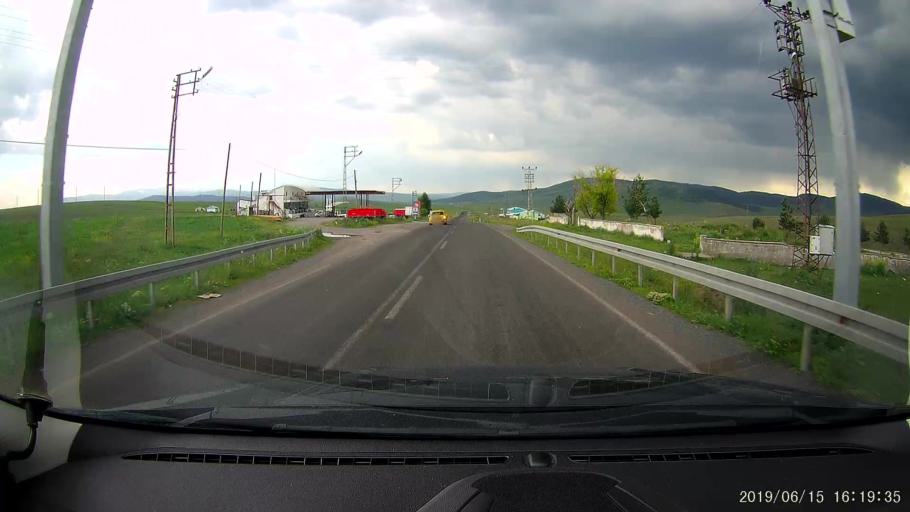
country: TR
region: Ardahan
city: Hanak
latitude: 41.2268
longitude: 42.8498
